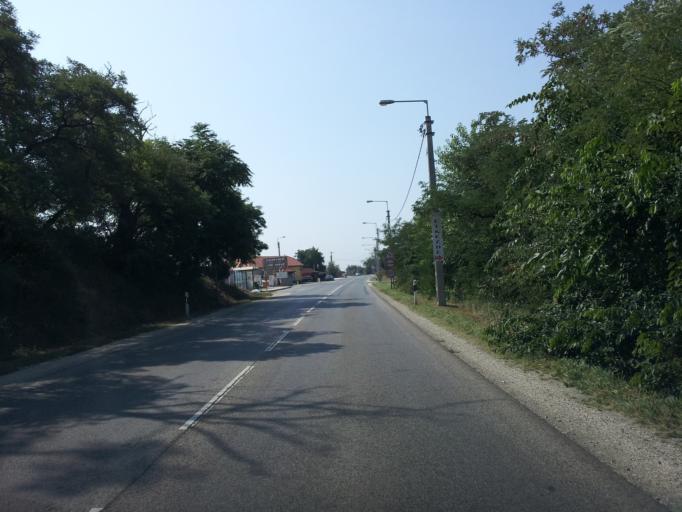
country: HU
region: Pest
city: Dunavarsany
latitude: 47.2931
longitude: 19.0303
